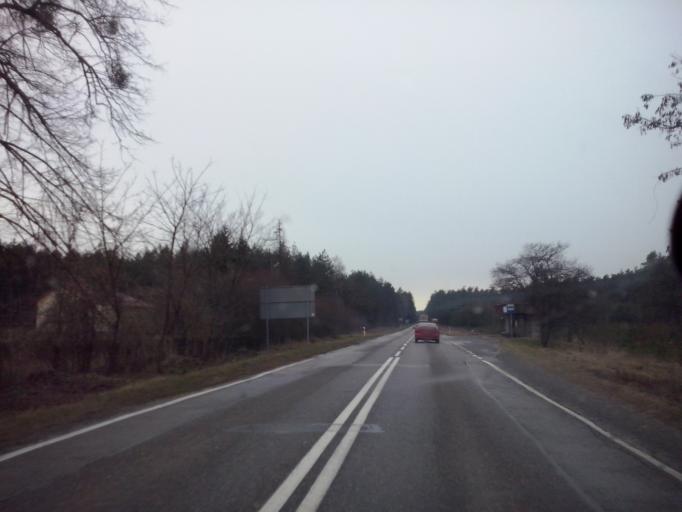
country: PL
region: Lublin Voivodeship
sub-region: Powiat bilgorajski
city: Tereszpol
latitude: 50.6016
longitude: 22.8759
